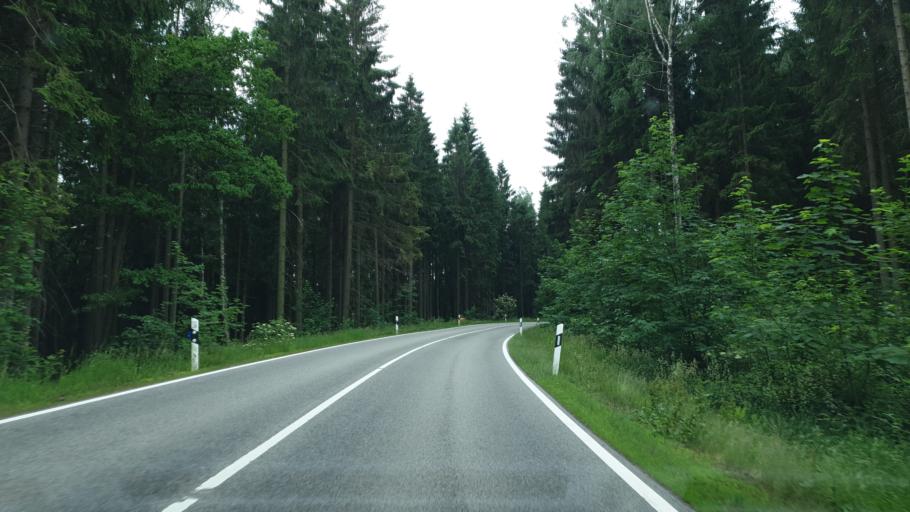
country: DE
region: Saxony
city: Auerbach
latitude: 50.4832
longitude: 12.4343
